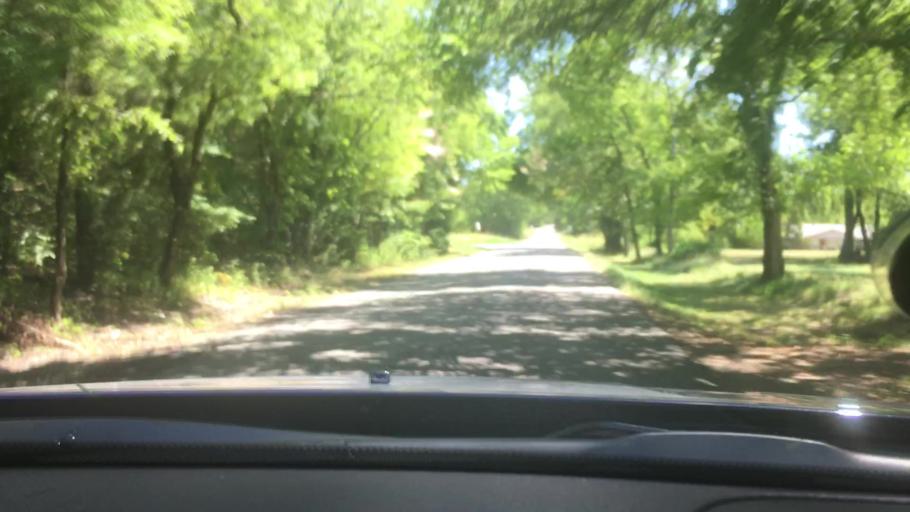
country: US
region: Oklahoma
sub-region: Bryan County
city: Durant
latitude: 33.9961
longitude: -96.2318
